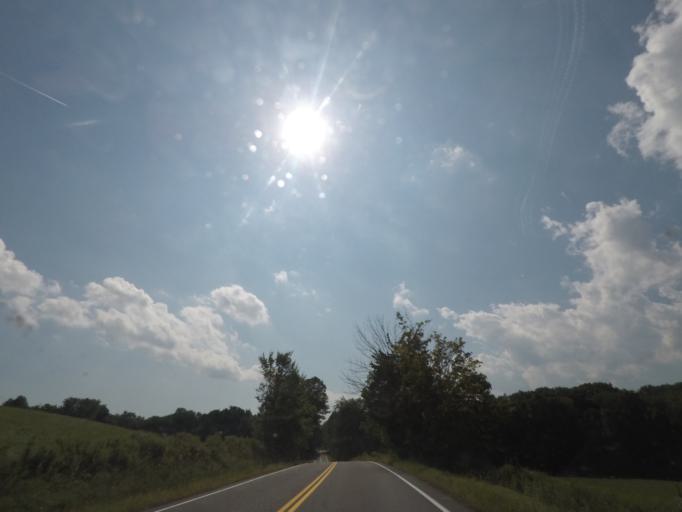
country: US
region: New York
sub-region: Rensselaer County
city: Poestenkill
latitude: 42.8088
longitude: -73.5153
